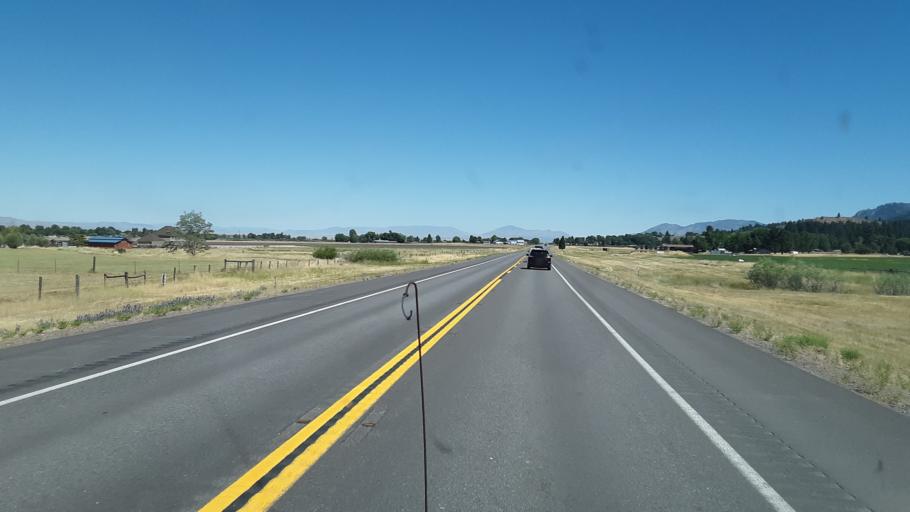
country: US
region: California
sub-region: Lassen County
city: Janesville
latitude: 40.3013
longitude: -120.5213
